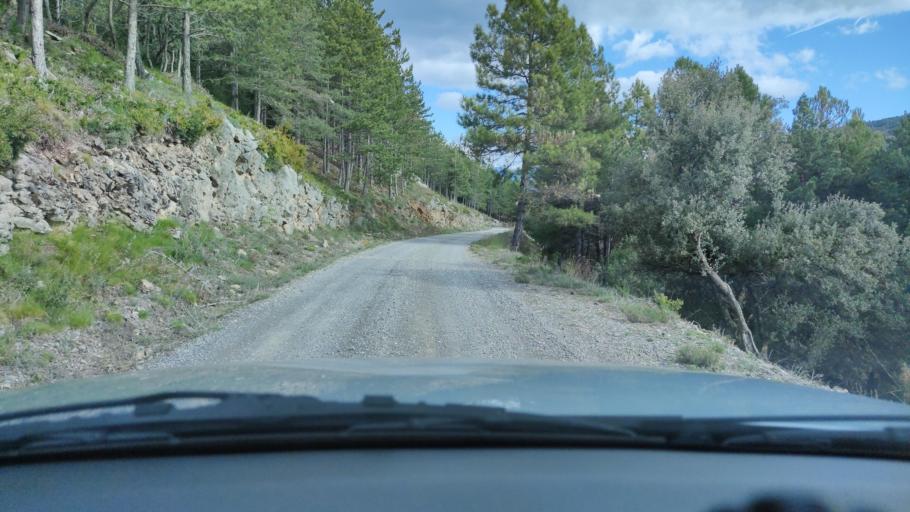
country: ES
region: Catalonia
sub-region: Provincia de Lleida
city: Coll de Nargo
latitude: 42.2446
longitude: 1.4089
